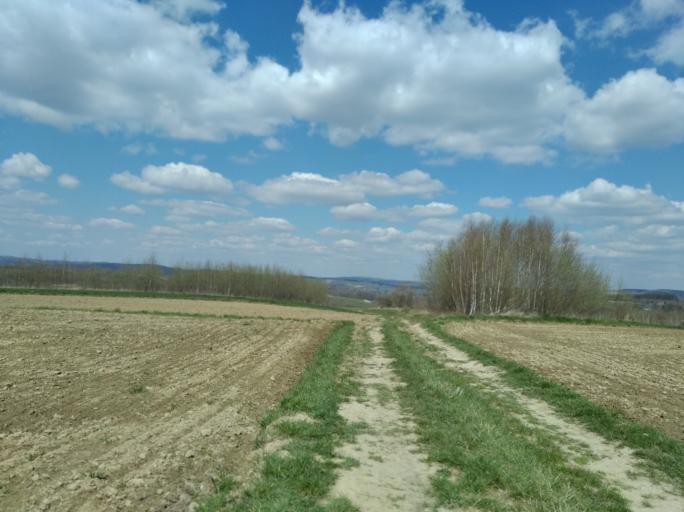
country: PL
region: Subcarpathian Voivodeship
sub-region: Powiat strzyzowski
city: Wysoka Strzyzowska
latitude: 49.8402
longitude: 21.7633
